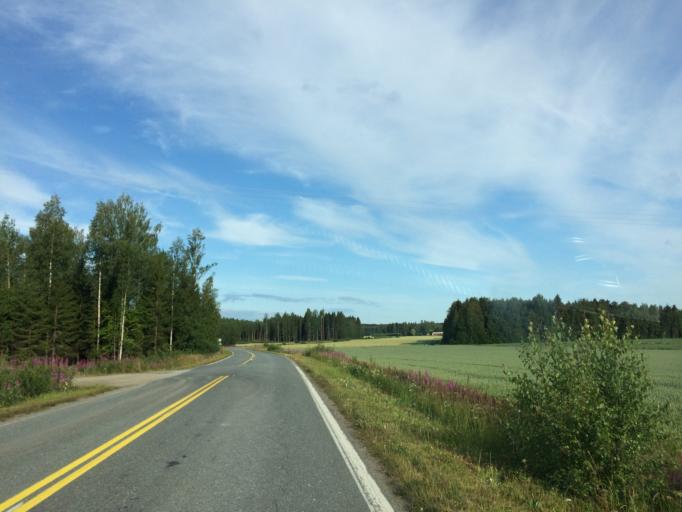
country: FI
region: Haeme
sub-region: Haemeenlinna
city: Janakkala
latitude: 60.9304
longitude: 24.5530
